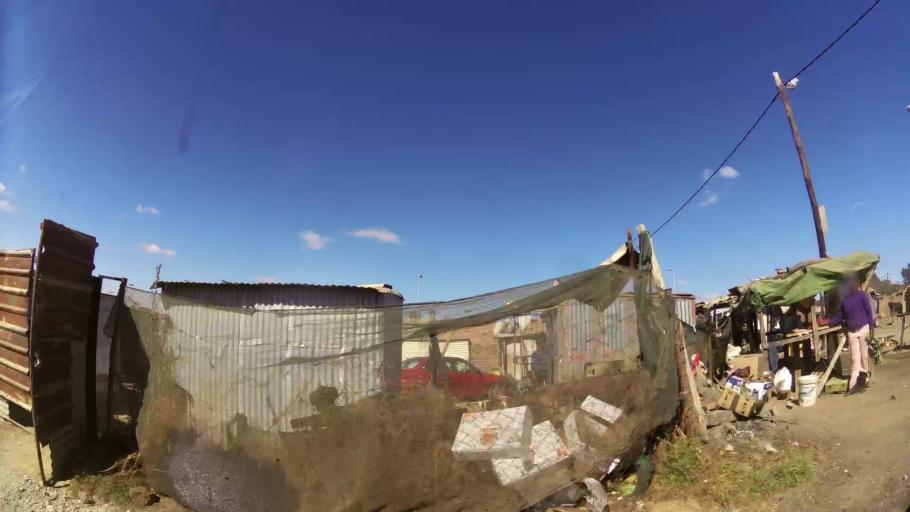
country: ZA
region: Gauteng
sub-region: City of Johannesburg Metropolitan Municipality
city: Midrand
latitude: -25.9227
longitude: 28.0919
